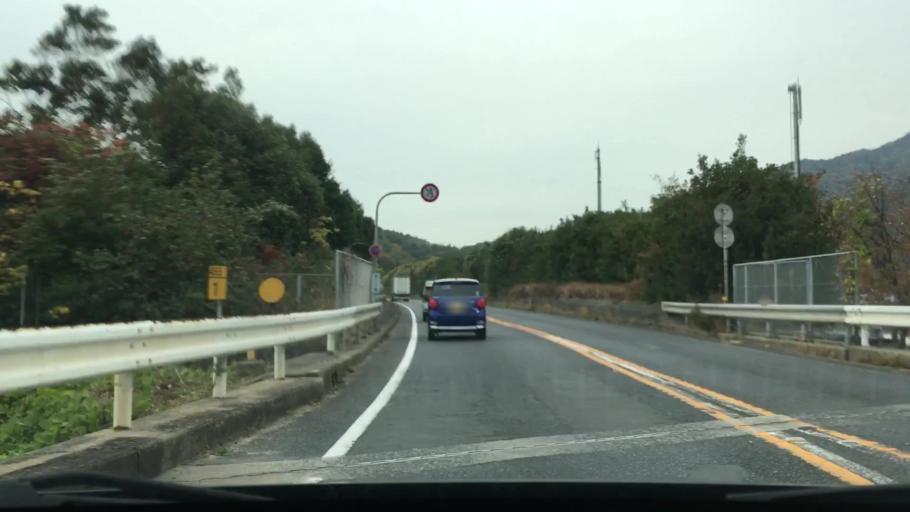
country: JP
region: Yamaguchi
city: Hofu
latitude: 34.0686
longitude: 131.6013
